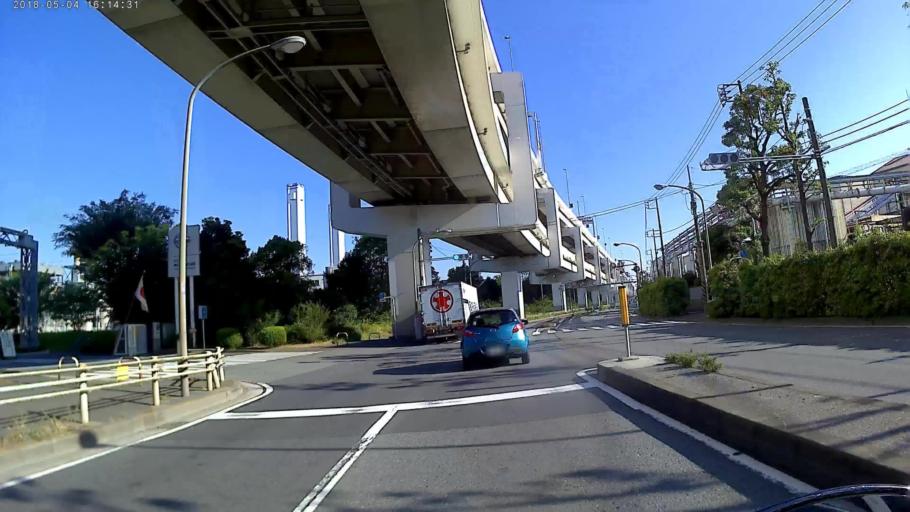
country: JP
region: Kanagawa
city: Yokohama
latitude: 35.4840
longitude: 139.6756
